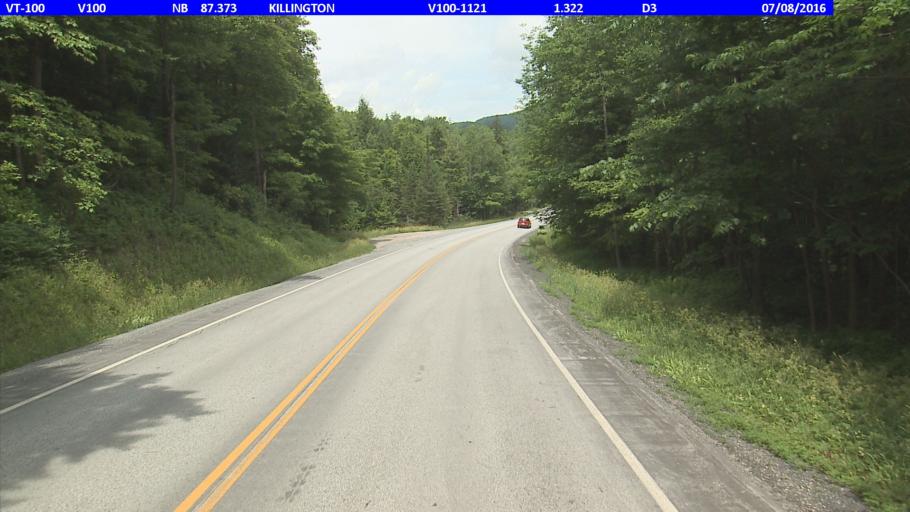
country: US
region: Vermont
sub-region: Rutland County
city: Rutland
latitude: 43.6850
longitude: -72.8137
